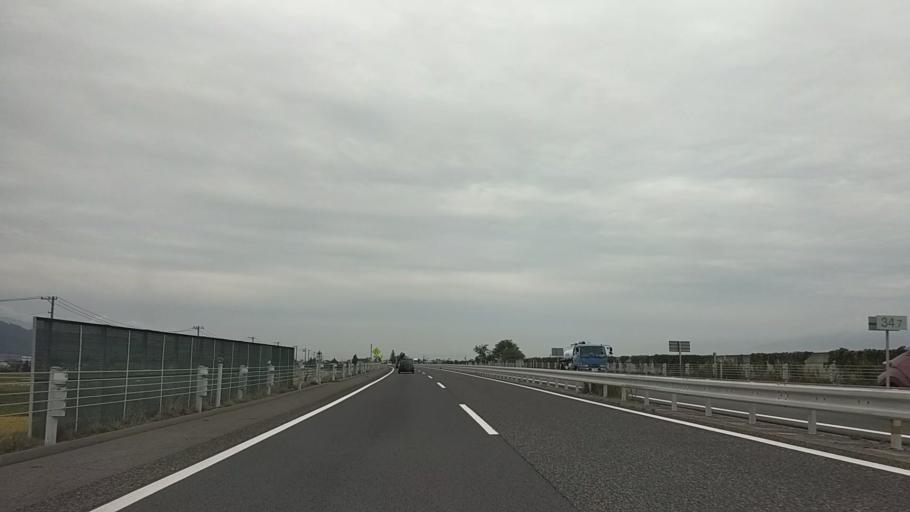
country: JP
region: Nagano
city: Toyoshina
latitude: 36.3129
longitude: 137.9206
